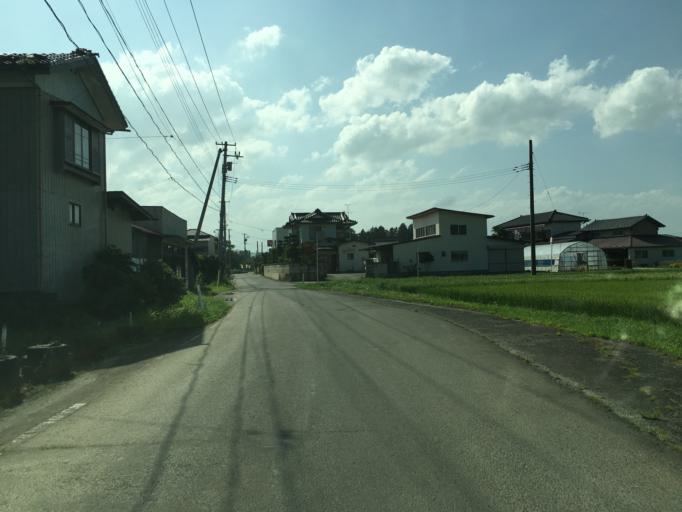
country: JP
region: Miyagi
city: Kakuda
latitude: 37.9430
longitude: 140.8077
